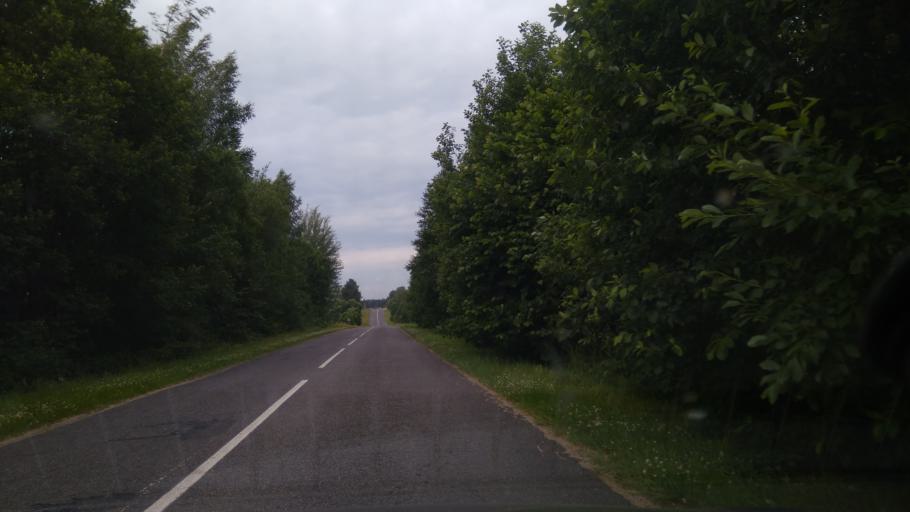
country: BY
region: Vitebsk
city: Lyepyel'
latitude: 54.9767
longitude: 28.8776
